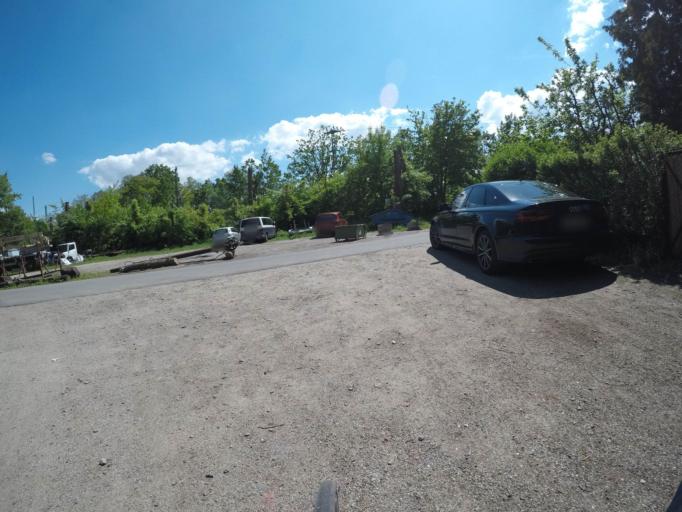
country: DE
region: Brandenburg
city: Werder
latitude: 52.3933
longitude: 12.9390
